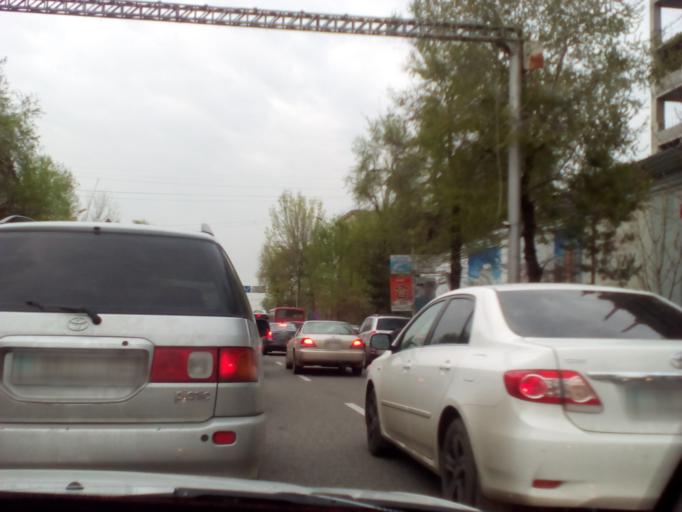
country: KZ
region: Almaty Qalasy
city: Almaty
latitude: 43.2687
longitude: 76.9450
